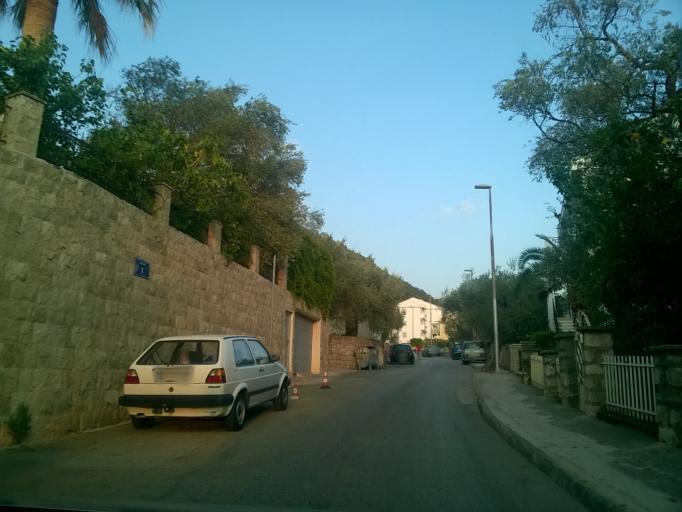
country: ME
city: Petrovac na Moru
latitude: 42.2062
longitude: 18.9443
